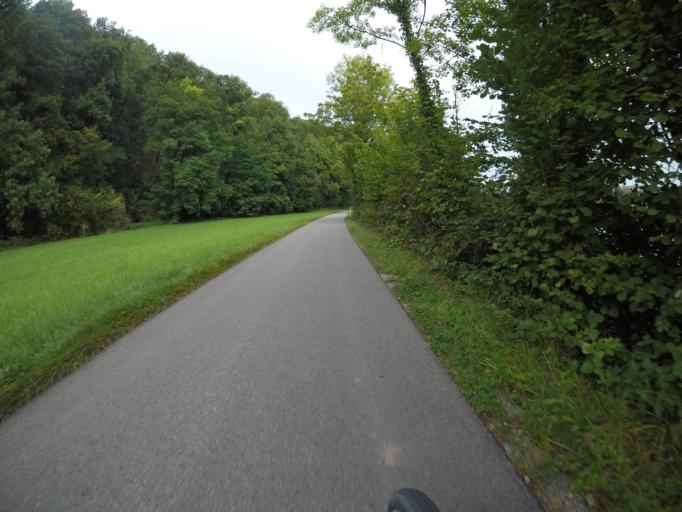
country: DE
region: Baden-Wuerttemberg
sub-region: Regierungsbezirk Stuttgart
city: Marbach am Neckar
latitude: 48.8975
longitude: 9.2567
